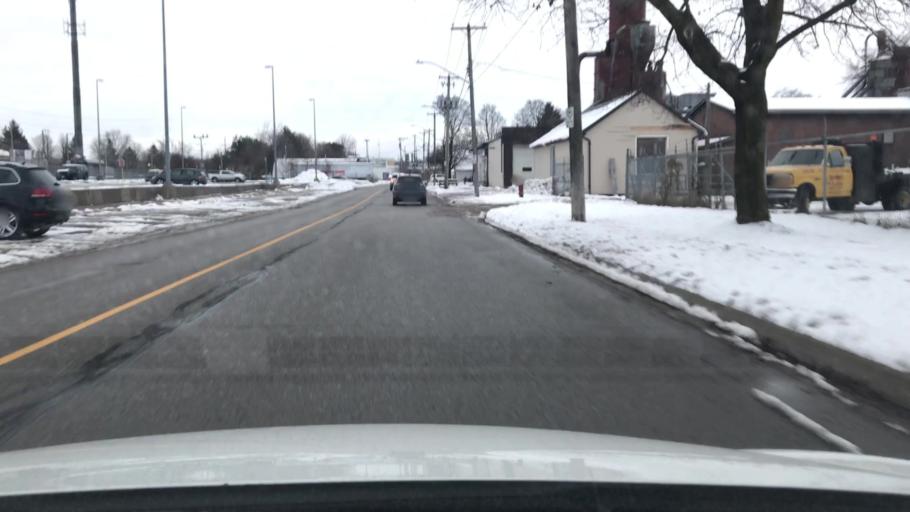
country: CA
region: Ontario
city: Newmarket
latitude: 43.9991
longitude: -79.4599
